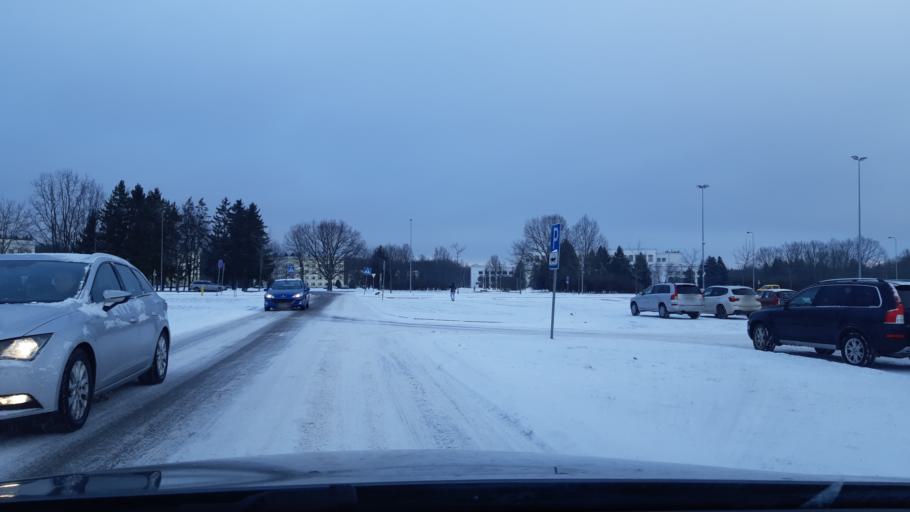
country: LT
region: Kauno apskritis
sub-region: Kauno rajonas
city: Akademija (Kaunas)
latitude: 54.8909
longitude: 23.8314
